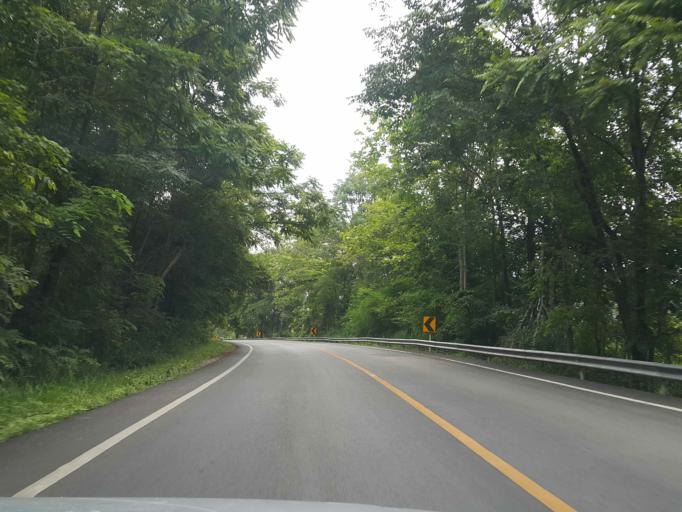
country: TH
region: Lampang
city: Thoen
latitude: 17.5521
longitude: 99.3385
